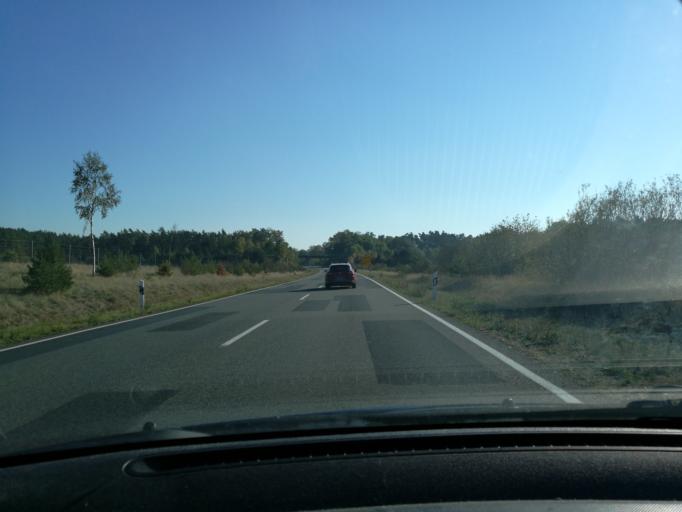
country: DE
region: Lower Saxony
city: Dahlem
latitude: 53.1810
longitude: 10.7646
